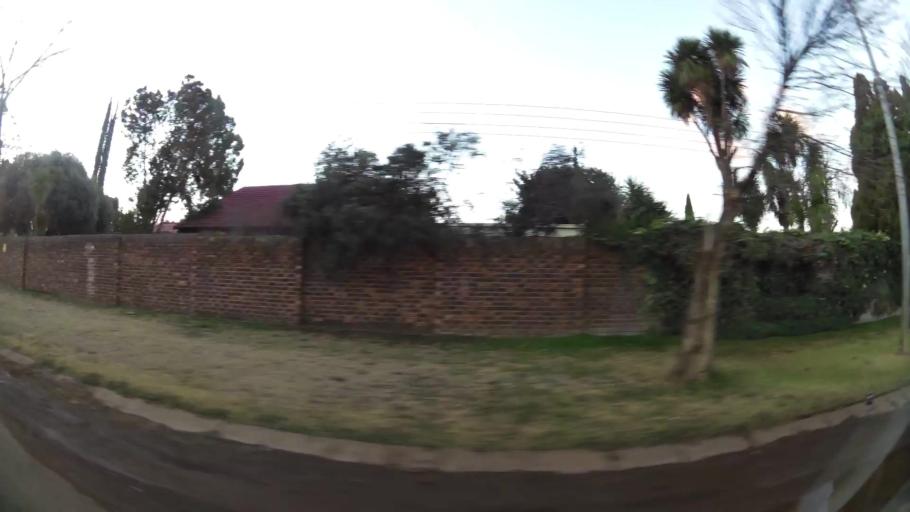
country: ZA
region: North-West
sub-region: Dr Kenneth Kaunda District Municipality
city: Potchefstroom
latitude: -26.7223
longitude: 27.1216
